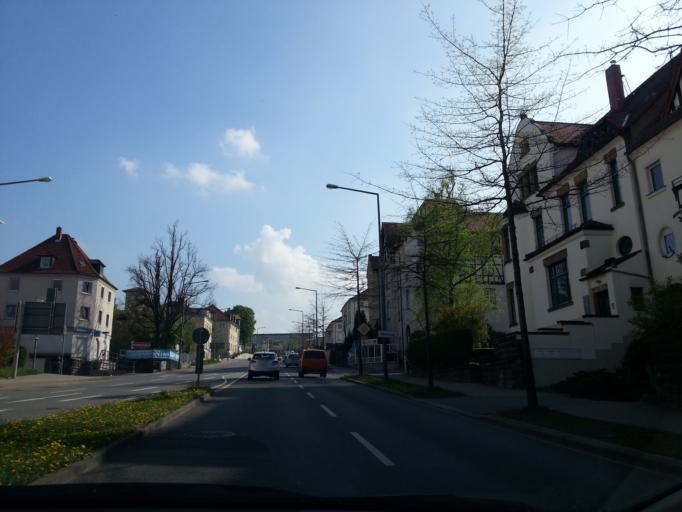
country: DE
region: Saxony
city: Dresden
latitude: 51.0271
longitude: 13.7314
